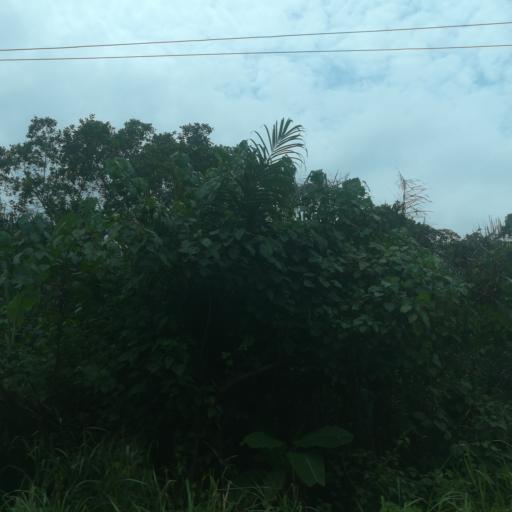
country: NG
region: Lagos
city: Ejirin
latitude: 6.6510
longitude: 3.7900
